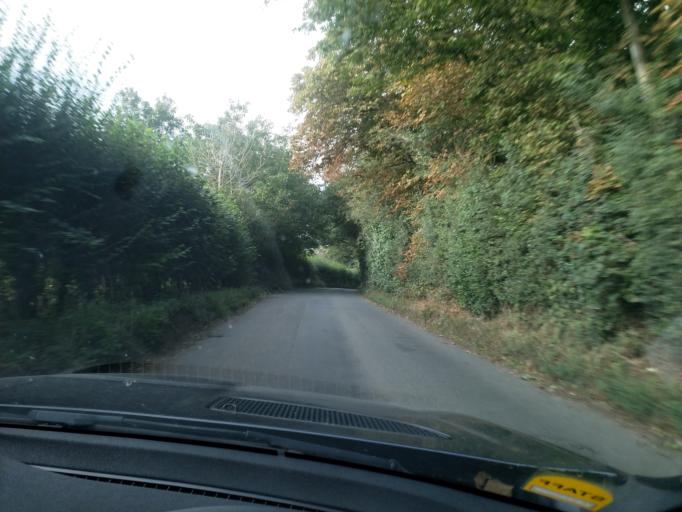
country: GB
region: England
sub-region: Suffolk
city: Elmswell
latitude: 52.2288
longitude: 0.9442
